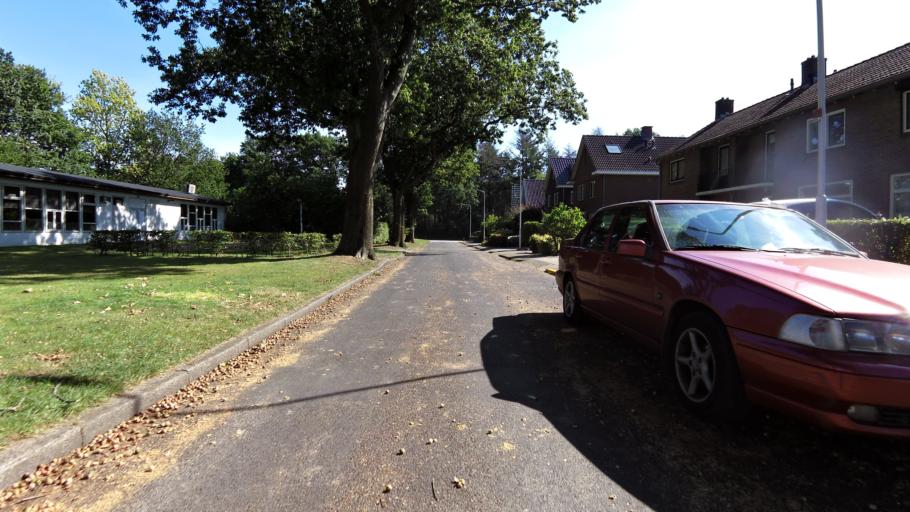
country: NL
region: Gelderland
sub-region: Gemeente Renkum
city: Heelsum
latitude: 51.9871
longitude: 5.7496
